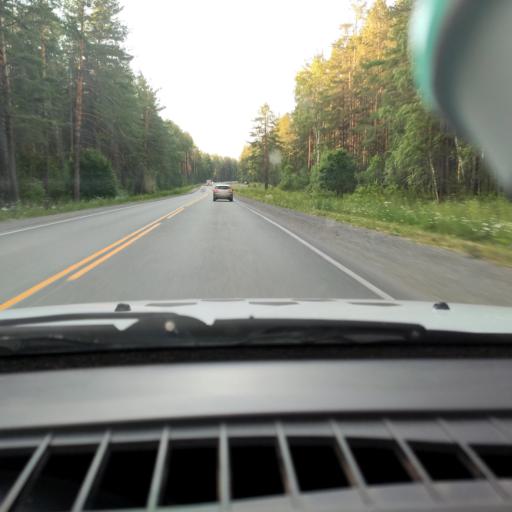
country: RU
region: Chelyabinsk
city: Turgoyak
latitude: 55.2743
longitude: 60.1973
